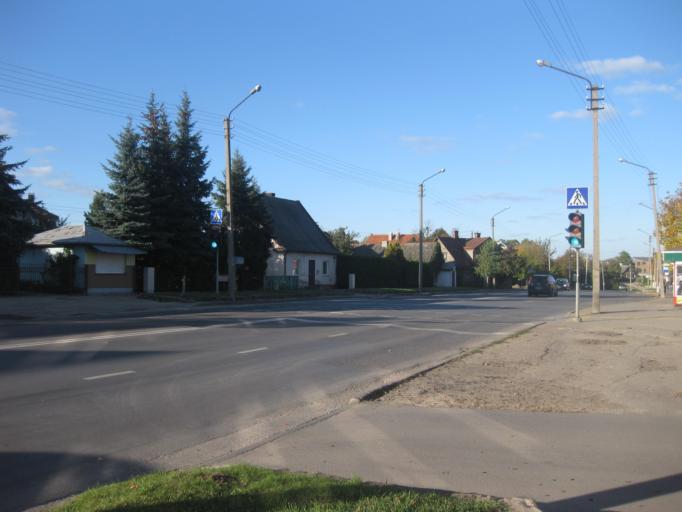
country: LT
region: Kauno apskritis
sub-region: Kaunas
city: Aleksotas
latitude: 54.8851
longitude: 23.8954
